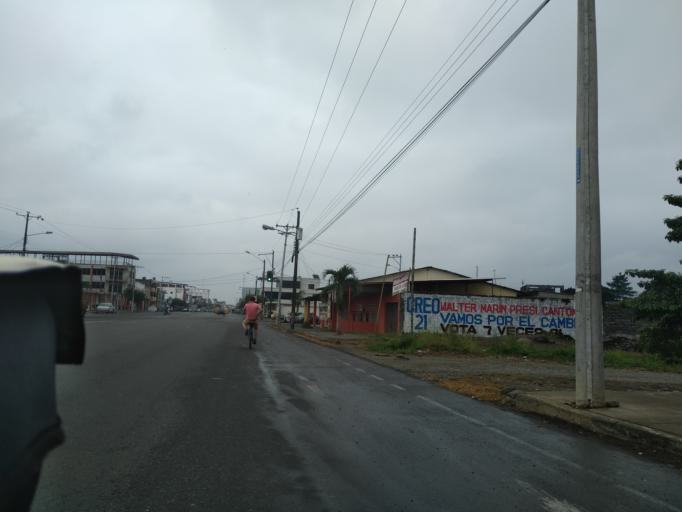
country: EC
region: Cotopaxi
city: La Mana
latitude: -0.9508
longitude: -79.3469
